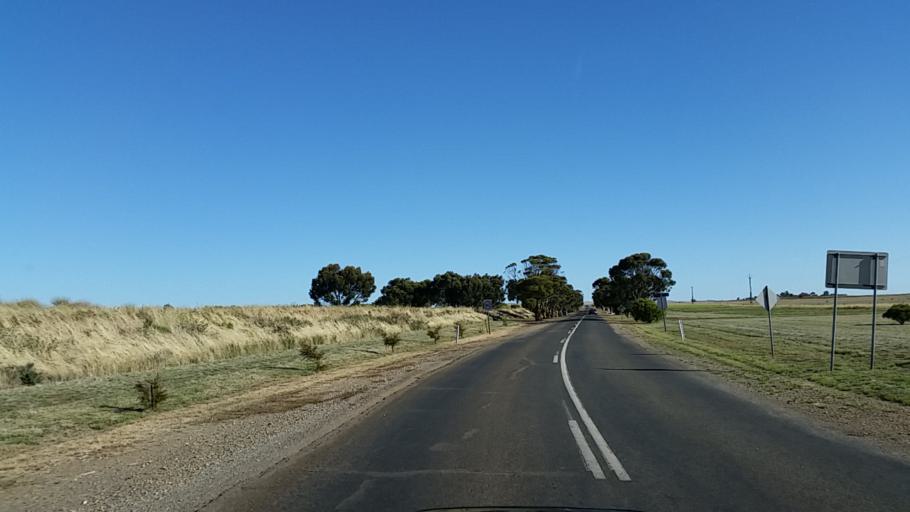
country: AU
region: South Australia
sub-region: Peterborough
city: Peterborough
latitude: -32.9780
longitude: 138.8455
